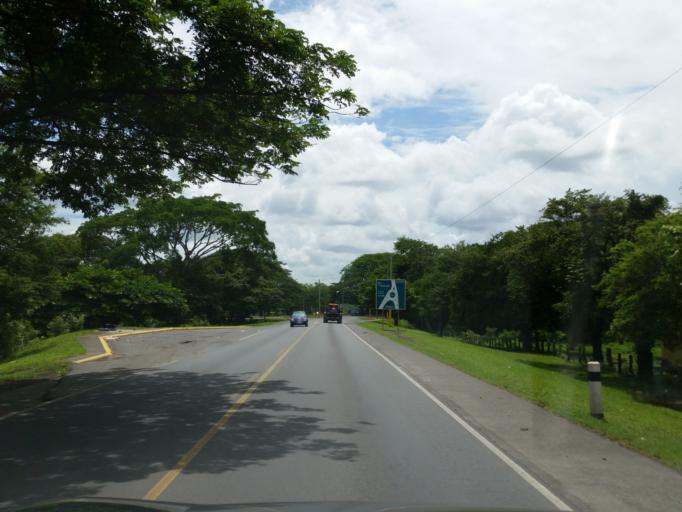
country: NI
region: Managua
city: Tipitapa
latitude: 12.1565
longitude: -86.1416
